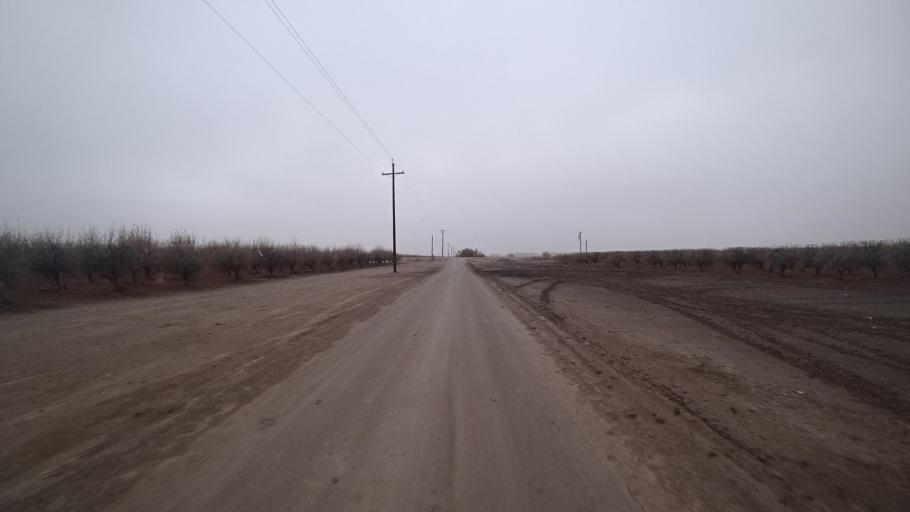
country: US
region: California
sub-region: Kern County
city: Lost Hills
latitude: 35.5868
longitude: -119.6160
